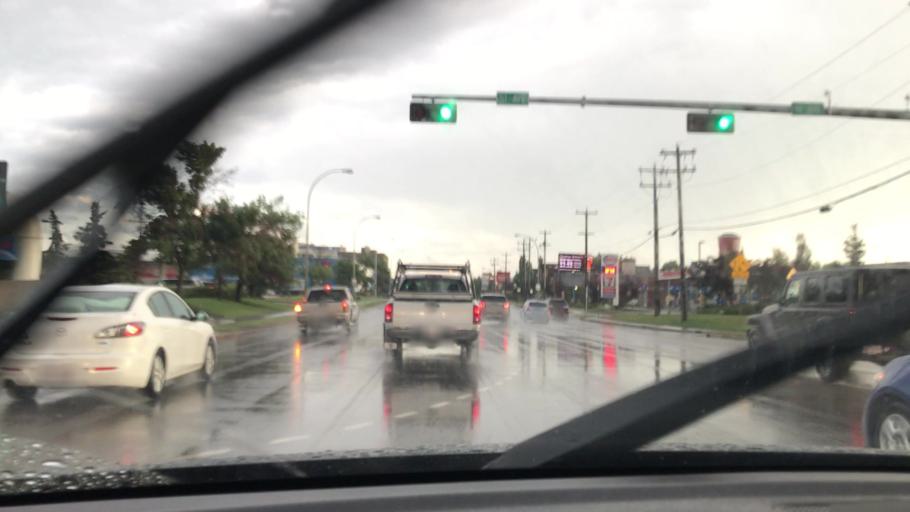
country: CA
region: Alberta
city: Edmonton
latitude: 53.4881
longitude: -113.4949
